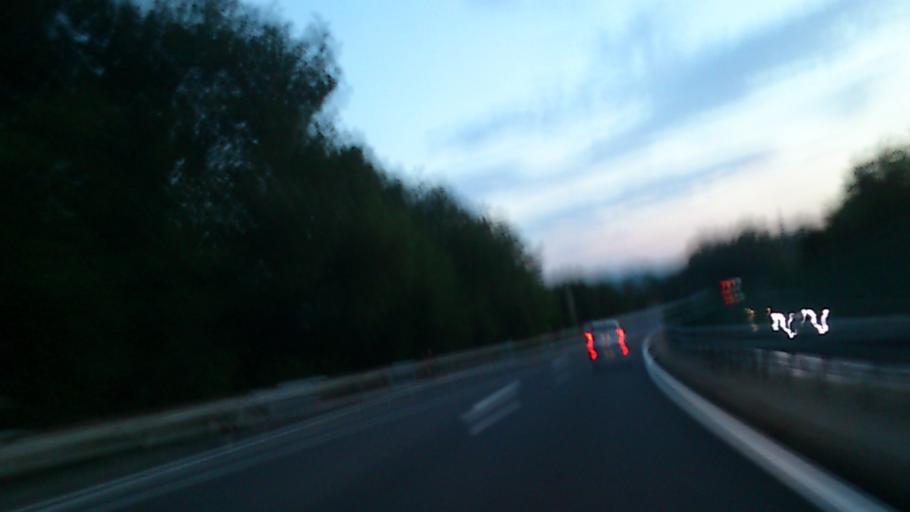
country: JP
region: Gifu
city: Tajimi
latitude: 35.3527
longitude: 137.1393
